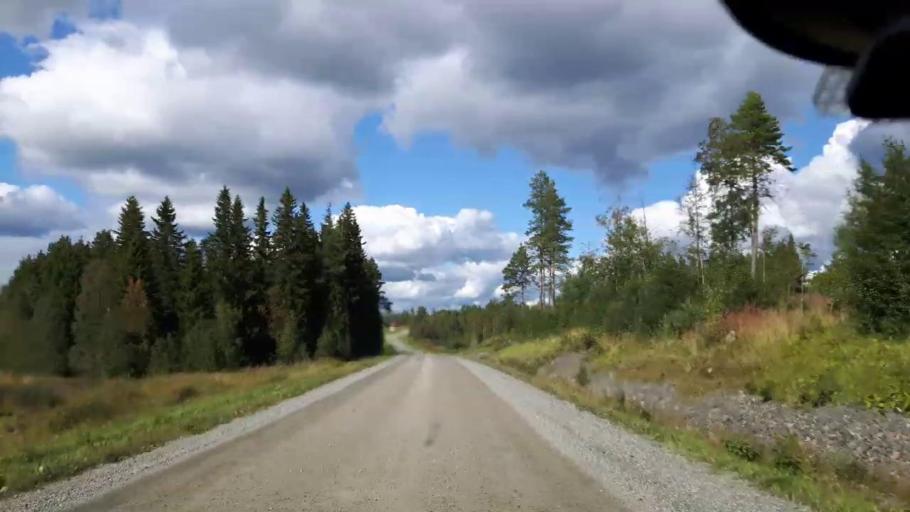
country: SE
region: Jaemtland
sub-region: Stroemsunds Kommun
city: Stroemsund
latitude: 63.3511
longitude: 15.5705
